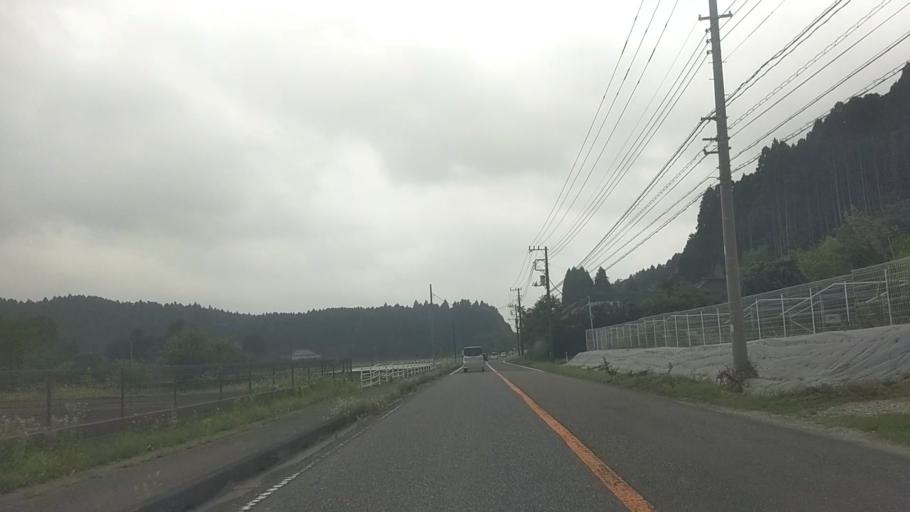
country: JP
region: Chiba
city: Ohara
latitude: 35.2724
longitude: 140.3313
